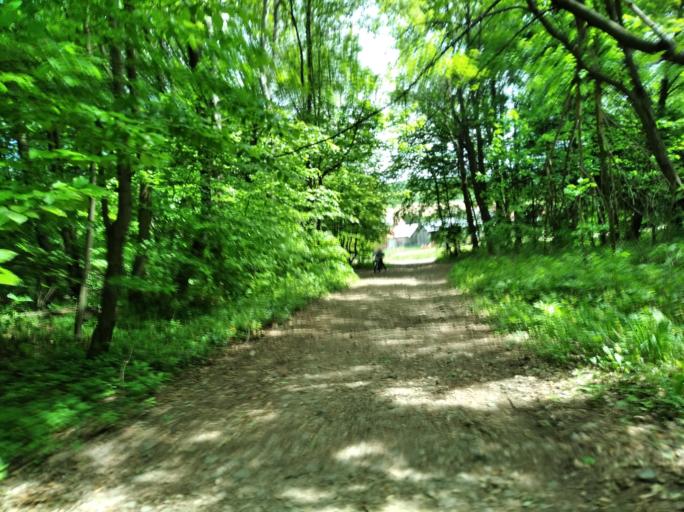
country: PL
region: Subcarpathian Voivodeship
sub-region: Powiat strzyzowski
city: Frysztak
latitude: 49.8917
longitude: 21.5606
